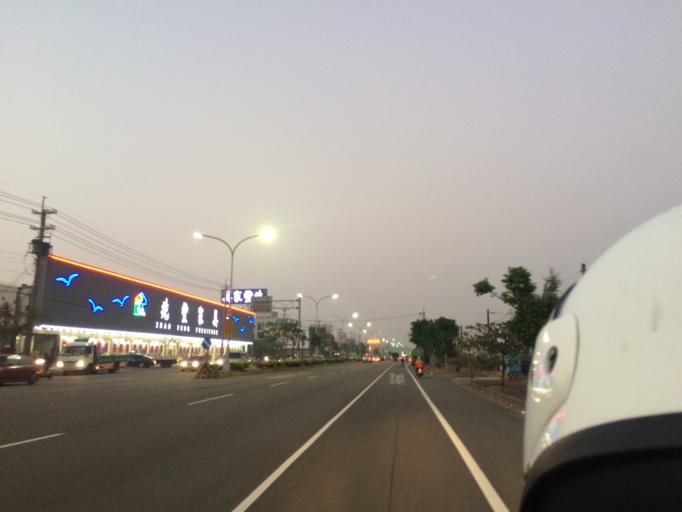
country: TW
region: Taiwan
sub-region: Hsinchu
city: Hsinchu
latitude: 24.7794
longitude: 120.9189
